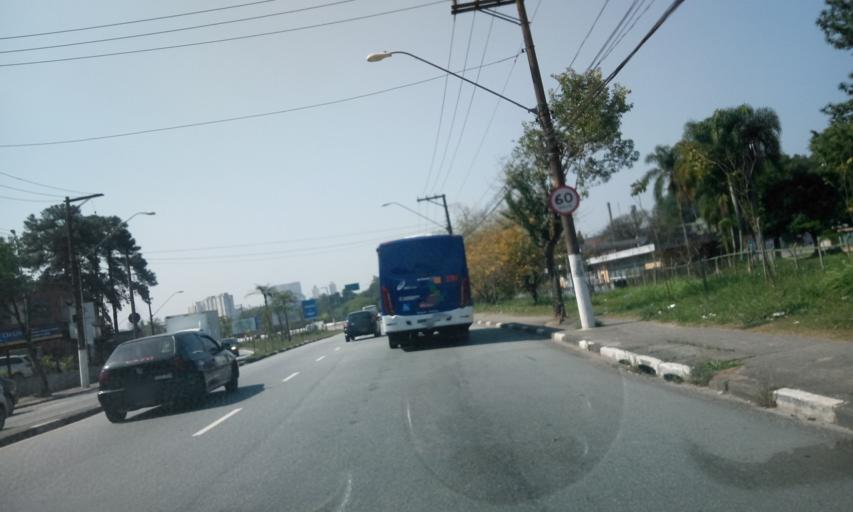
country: BR
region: Sao Paulo
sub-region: Sao Bernardo Do Campo
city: Sao Bernardo do Campo
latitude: -23.7340
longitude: -46.5531
